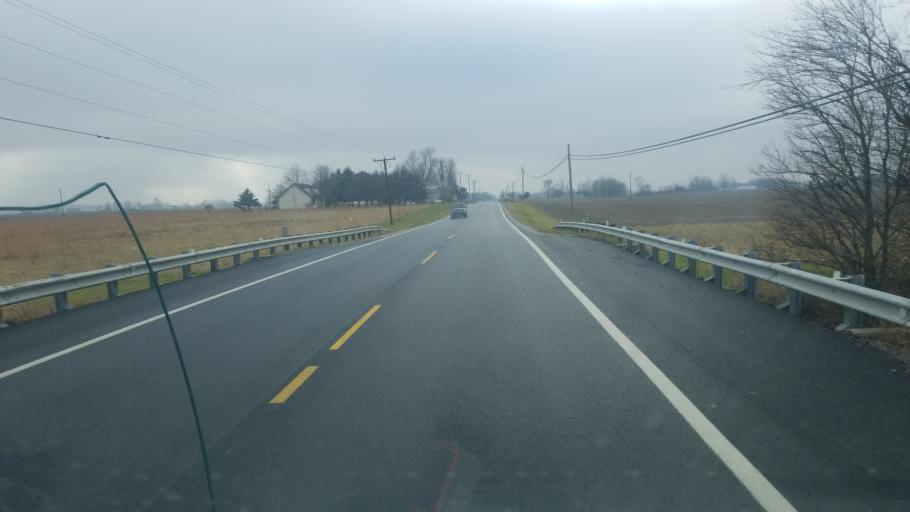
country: US
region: Ohio
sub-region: Hardin County
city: Kenton
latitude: 40.6748
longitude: -83.5284
